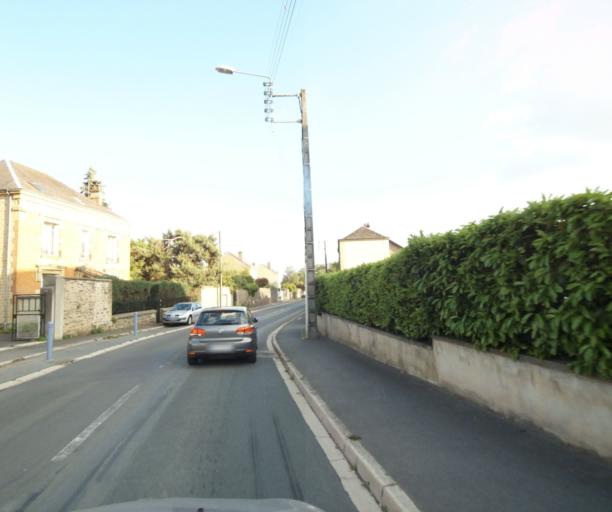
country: FR
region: Champagne-Ardenne
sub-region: Departement des Ardennes
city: Charleville-Mezieres
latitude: 49.7820
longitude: 4.7155
